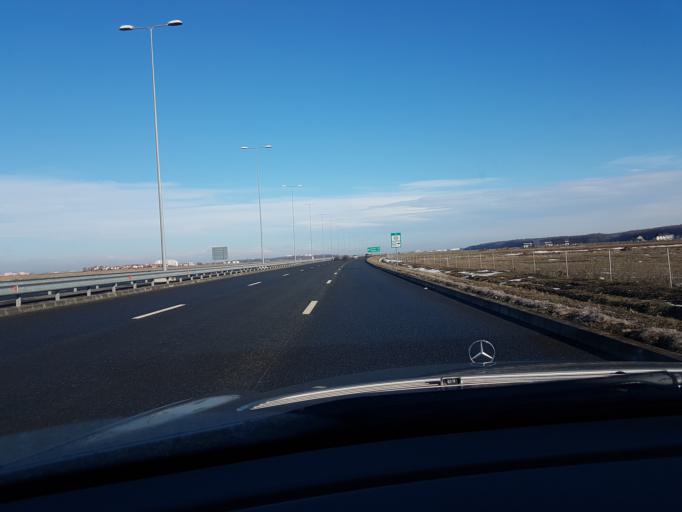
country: RO
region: Ilfov
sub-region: Voluntari City
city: Voluntari
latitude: 44.4993
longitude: 26.1537
